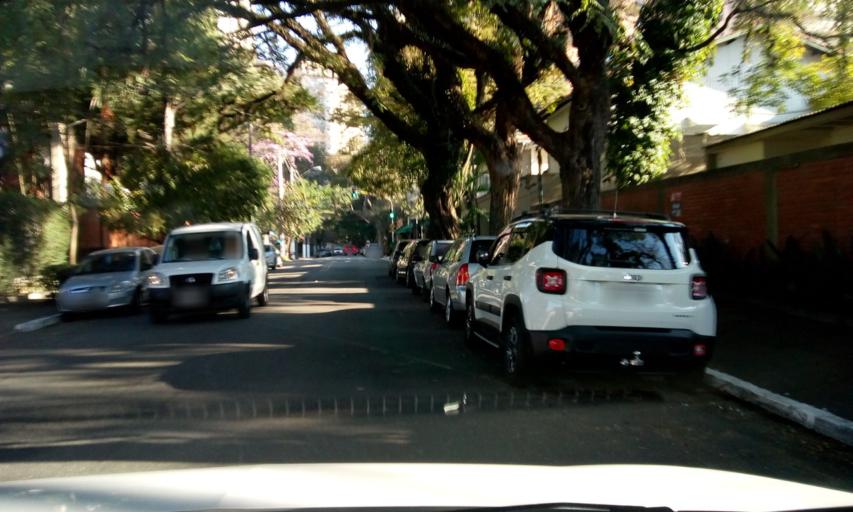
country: BR
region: Sao Paulo
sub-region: Sao Paulo
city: Sao Paulo
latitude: -23.5904
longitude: -46.6671
